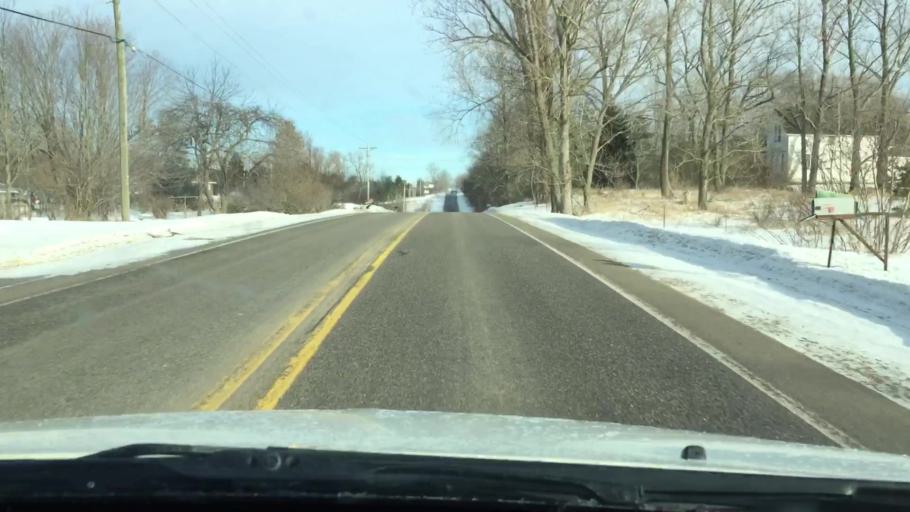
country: US
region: Michigan
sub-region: Kalkaska County
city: Kalkaska
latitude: 44.6408
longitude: -85.2286
